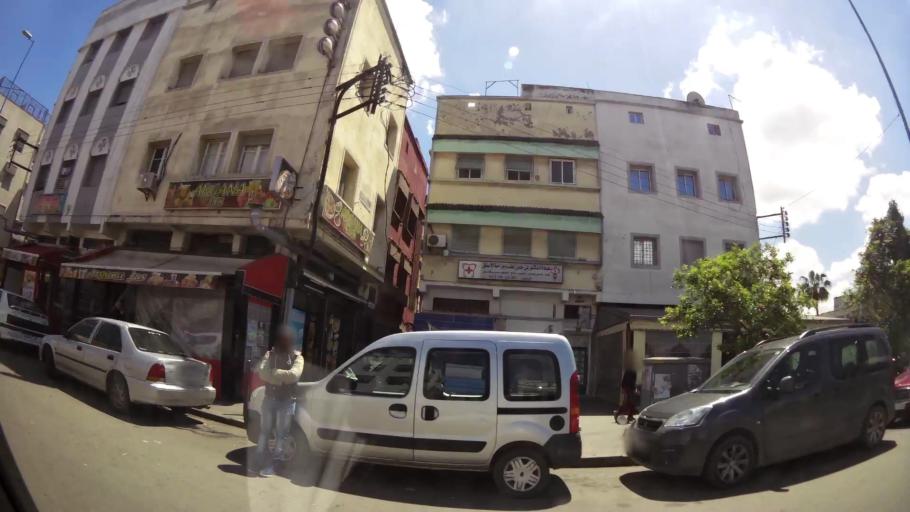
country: MA
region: Grand Casablanca
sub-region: Casablanca
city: Casablanca
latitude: 33.5565
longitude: -7.5719
